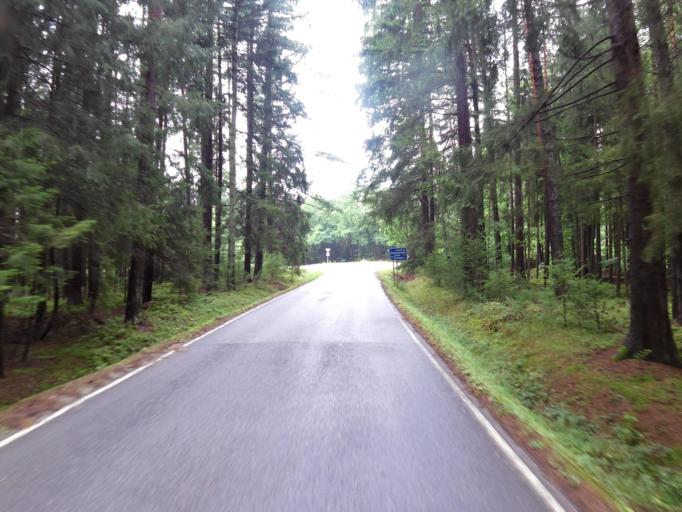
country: CZ
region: Jihocesky
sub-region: Okres Ceske Budejovice
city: Nove Hrady
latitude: 48.8386
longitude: 14.8066
